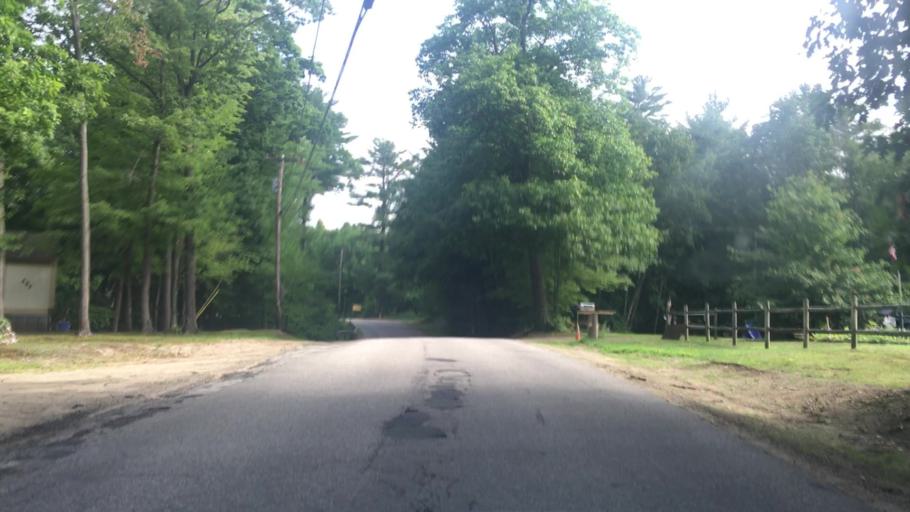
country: US
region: Maine
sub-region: Oxford County
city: South Paris
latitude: 44.1910
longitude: -70.5152
